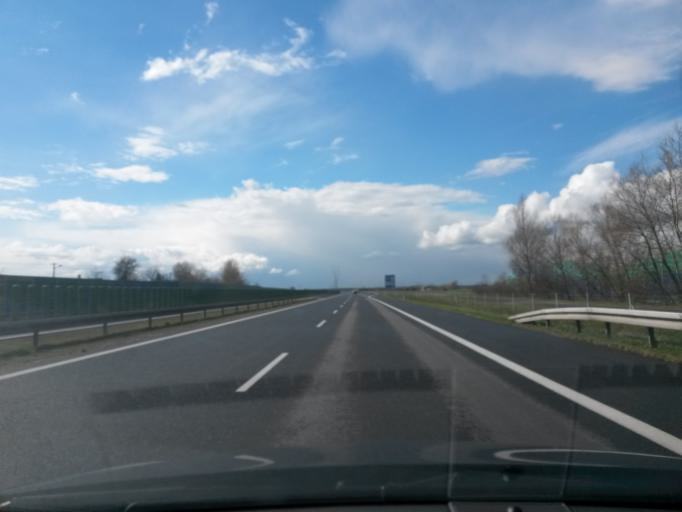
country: PL
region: Greater Poland Voivodeship
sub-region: Powiat wrzesinski
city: Kolaczkowo
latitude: 52.2923
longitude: 17.6614
